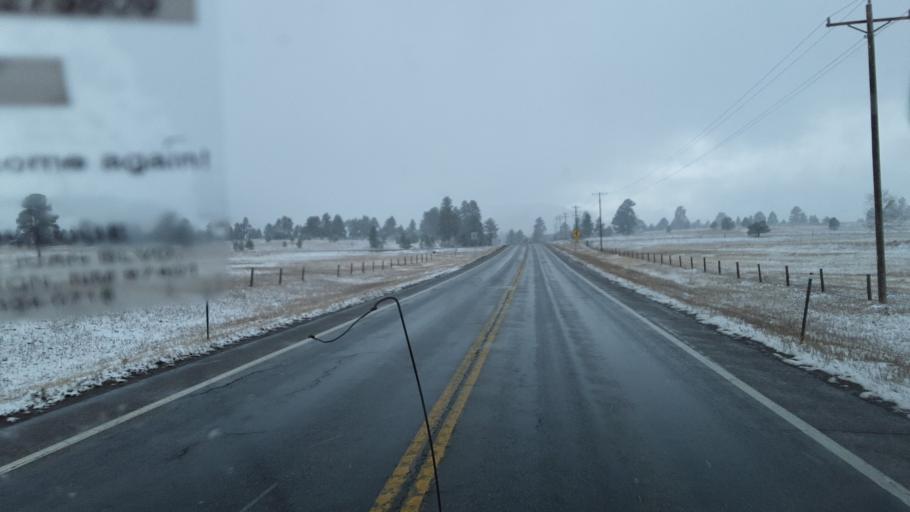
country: US
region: Colorado
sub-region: Archuleta County
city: Pagosa Springs
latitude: 37.2460
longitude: -107.0927
